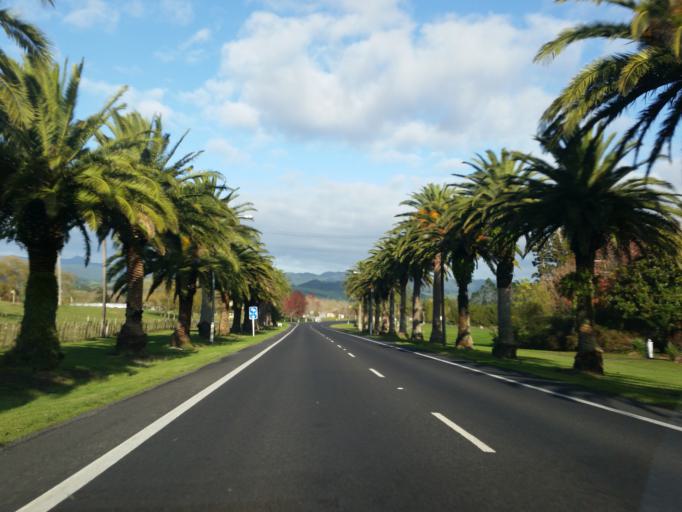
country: NZ
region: Waikato
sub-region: Hauraki District
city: Waihi
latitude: -37.3982
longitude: 175.8264
